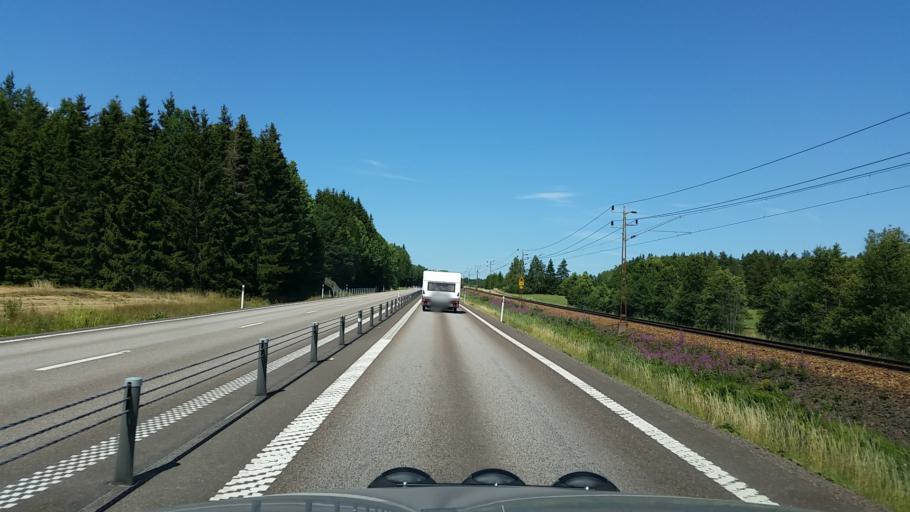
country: SE
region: Vaestra Goetaland
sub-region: Melleruds Kommun
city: Mellerud
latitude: 58.8591
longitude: 12.5582
